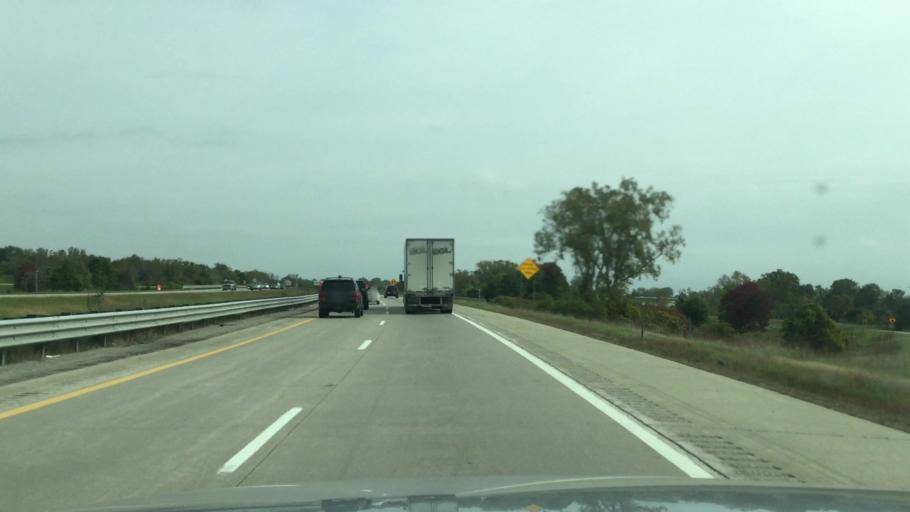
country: US
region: Michigan
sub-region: Genesee County
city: Swartz Creek
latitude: 42.9712
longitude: -83.7683
